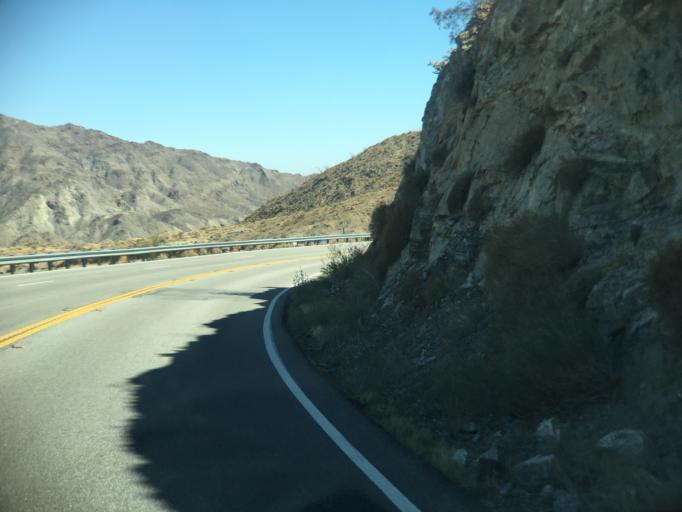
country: US
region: California
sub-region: Riverside County
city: Palm Desert
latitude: 33.6553
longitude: -116.4002
